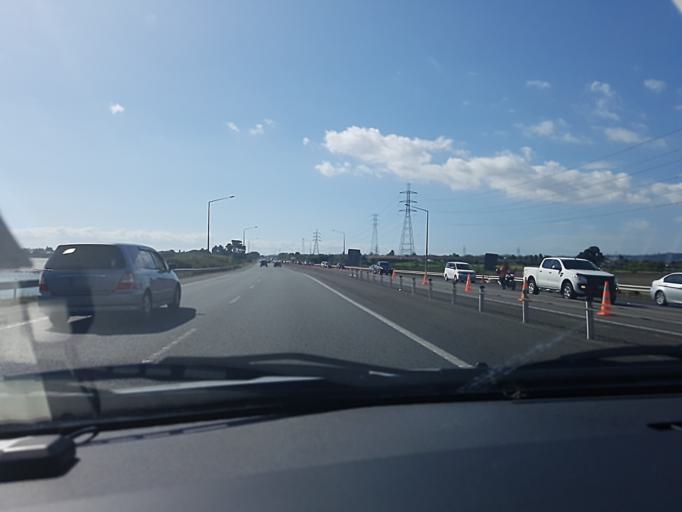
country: NZ
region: Auckland
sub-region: Auckland
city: Papakura
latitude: -37.0604
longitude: 174.9235
